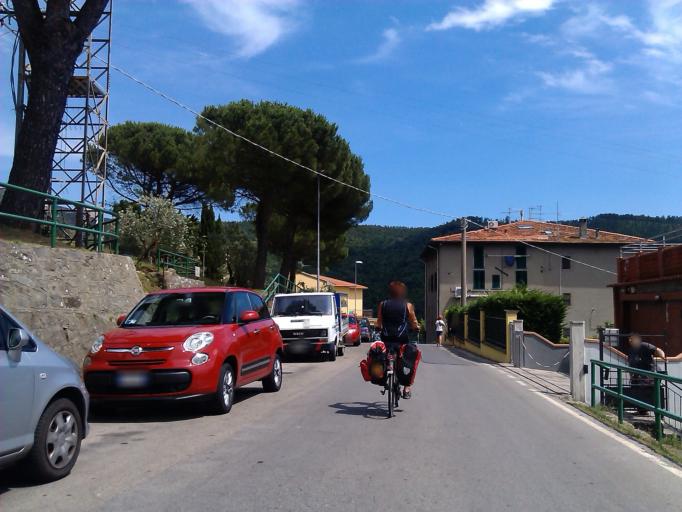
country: IT
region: Tuscany
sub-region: Provincia di Prato
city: Montemurlo
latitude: 43.9612
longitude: 11.0417
